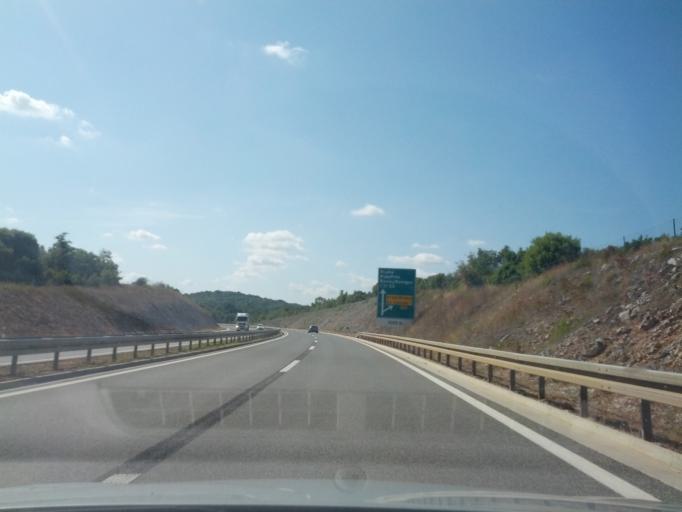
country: HR
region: Istarska
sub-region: Grad Rovinj
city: Rovinj
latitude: 45.1581
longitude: 13.7299
